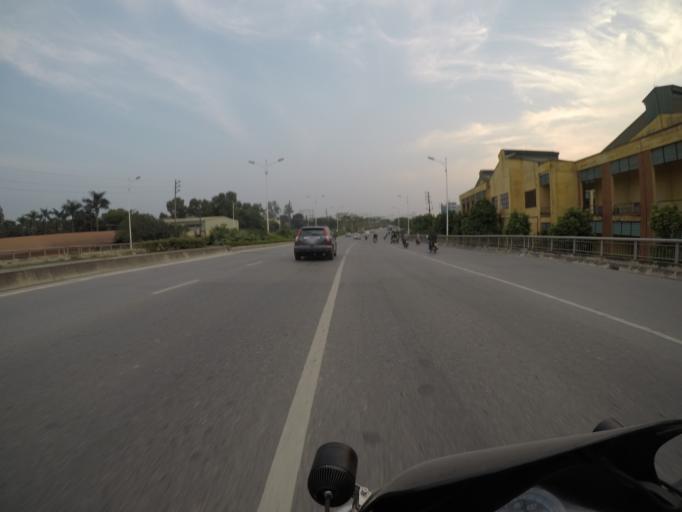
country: VN
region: Ha Noi
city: Trau Quy
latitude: 21.0341
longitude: 105.9015
